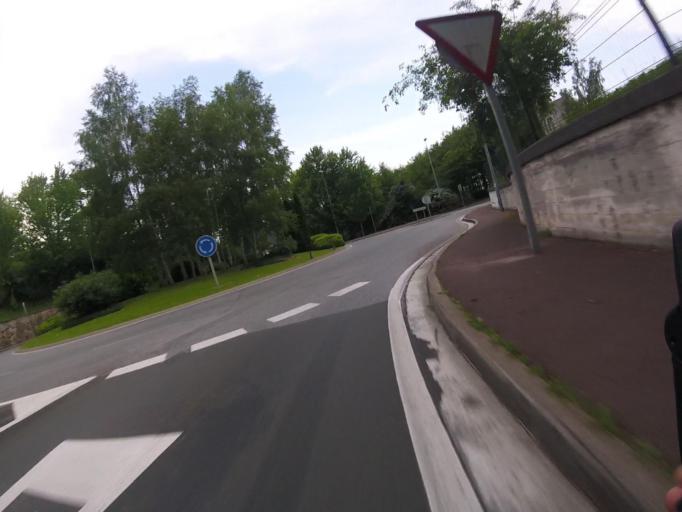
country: ES
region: Basque Country
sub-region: Provincia de Guipuzcoa
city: Errenteria
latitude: 43.3022
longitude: -1.9049
